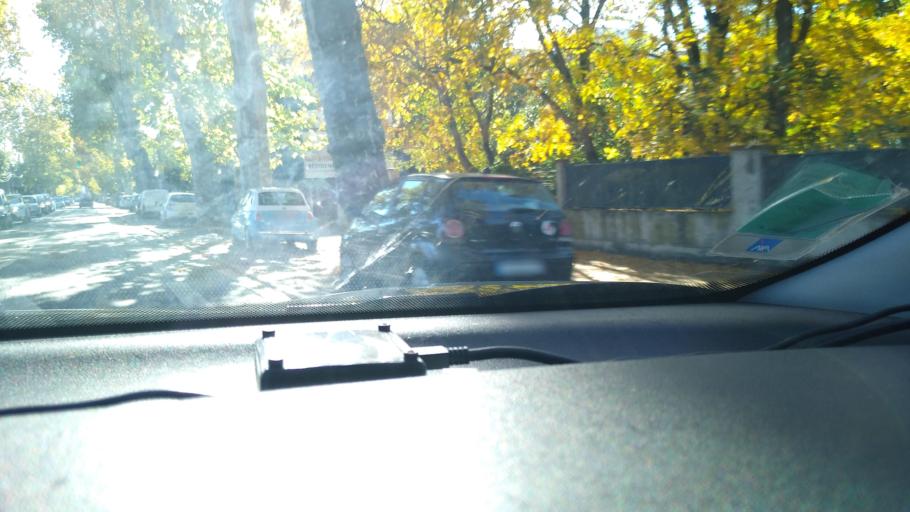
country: FR
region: Midi-Pyrenees
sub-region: Departement de la Haute-Garonne
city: L'Union
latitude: 43.6401
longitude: 1.4660
